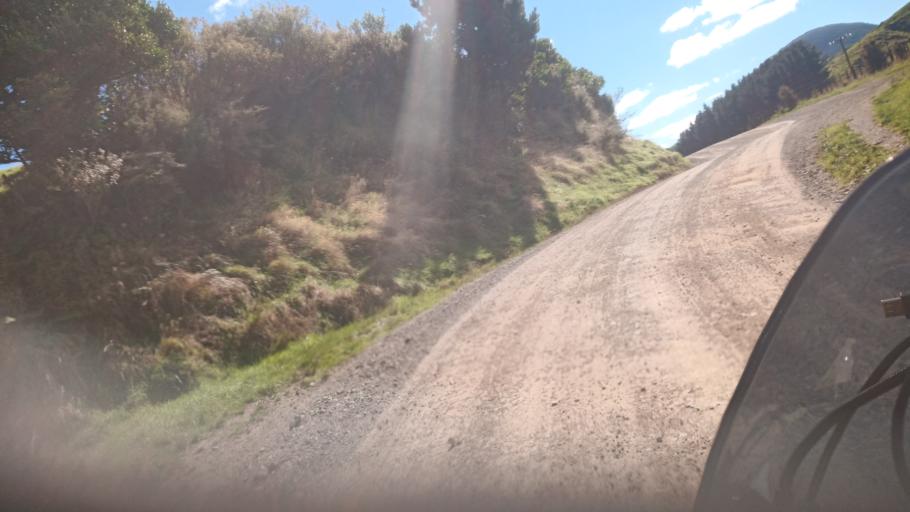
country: NZ
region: Bay of Plenty
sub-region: Opotiki District
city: Opotiki
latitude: -38.3361
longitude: 177.5788
